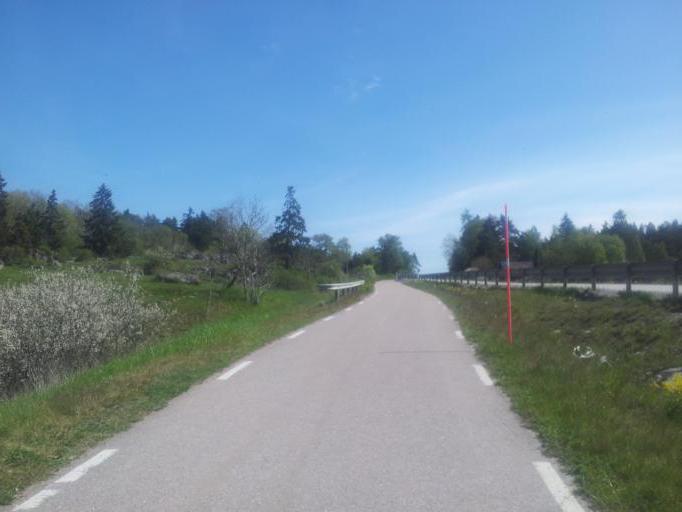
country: SE
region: Uppsala
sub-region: Uppsala Kommun
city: Saevja
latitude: 59.8484
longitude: 17.7730
